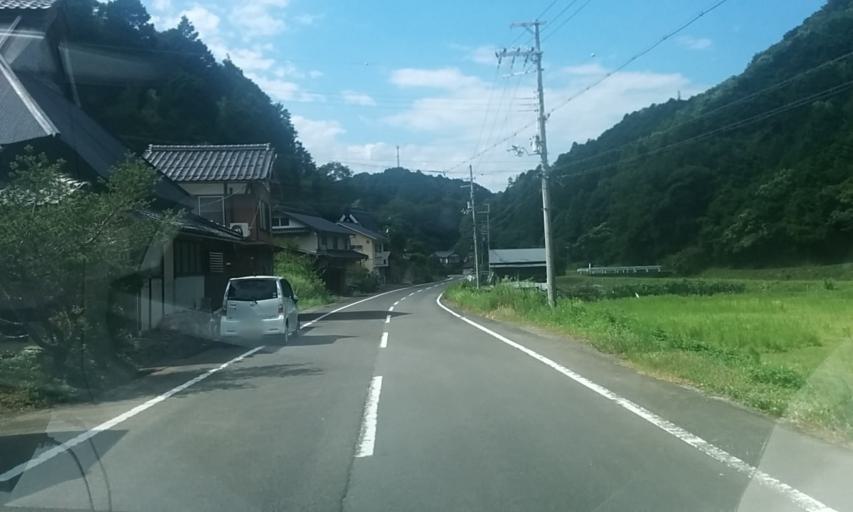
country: JP
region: Kyoto
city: Fukuchiyama
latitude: 35.3691
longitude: 135.1605
